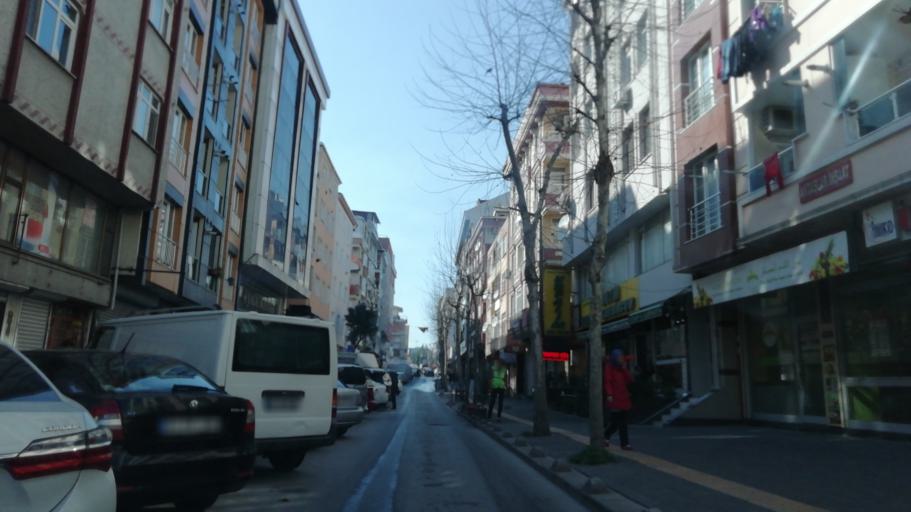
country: TR
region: Istanbul
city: Bahcelievler
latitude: 40.9943
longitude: 28.8385
